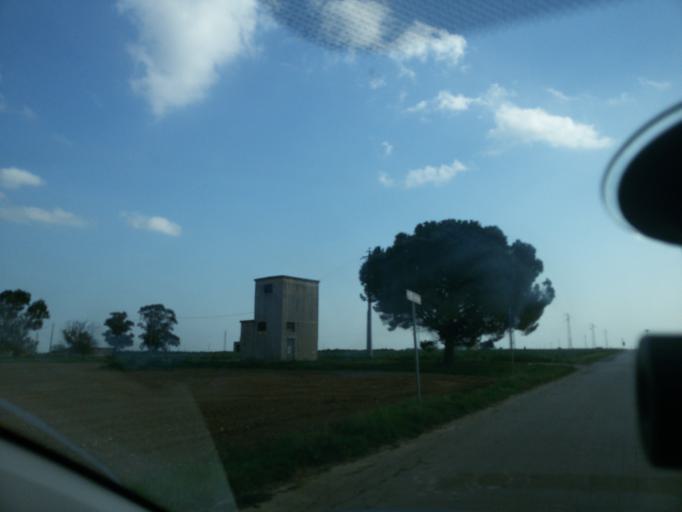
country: IT
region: Apulia
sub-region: Provincia di Brindisi
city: Mesagne
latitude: 40.6451
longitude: 17.8154
